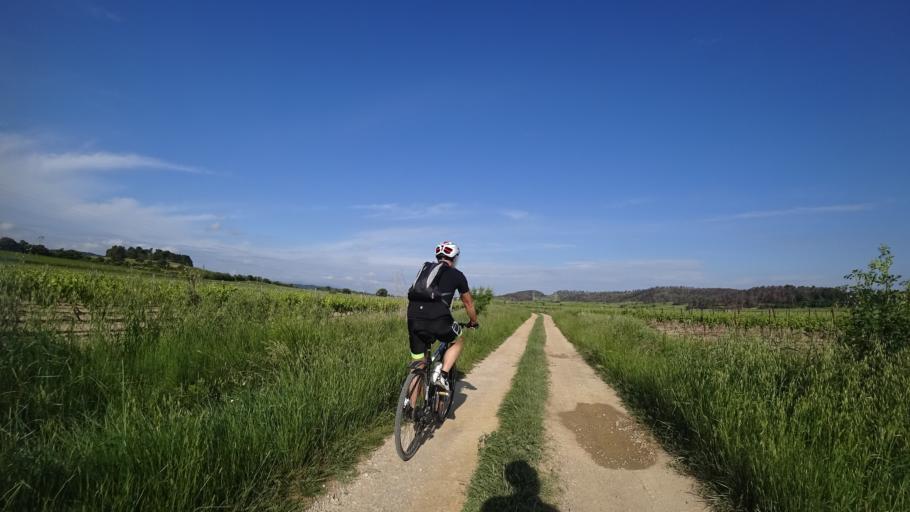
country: FR
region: Languedoc-Roussillon
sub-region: Departement de l'Herault
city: Olonzac
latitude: 43.2376
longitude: 2.7243
